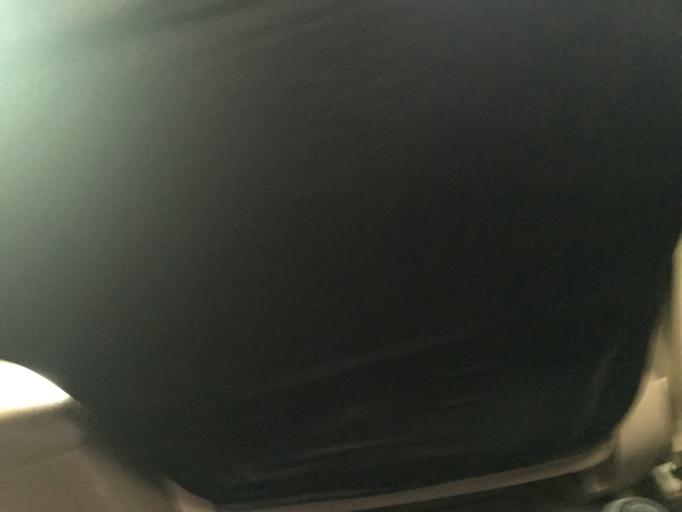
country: GY
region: Demerara-Mahaica
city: Georgetown
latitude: 6.8066
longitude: -58.1163
